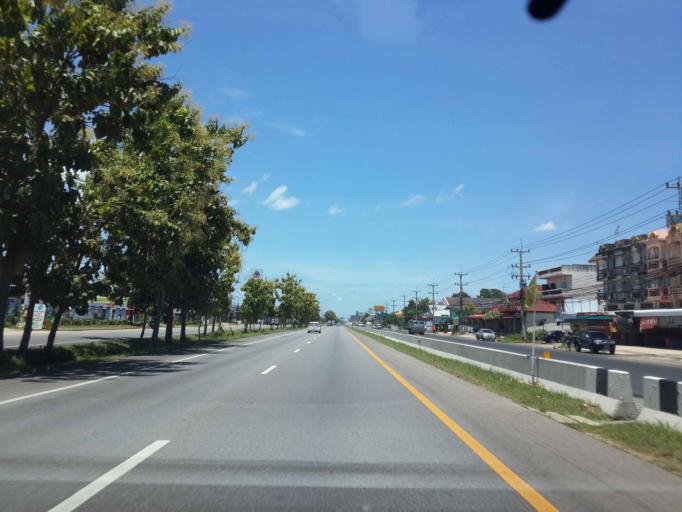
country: TH
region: Phetchaburi
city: Khao Yoi
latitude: 13.2938
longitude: 99.8228
